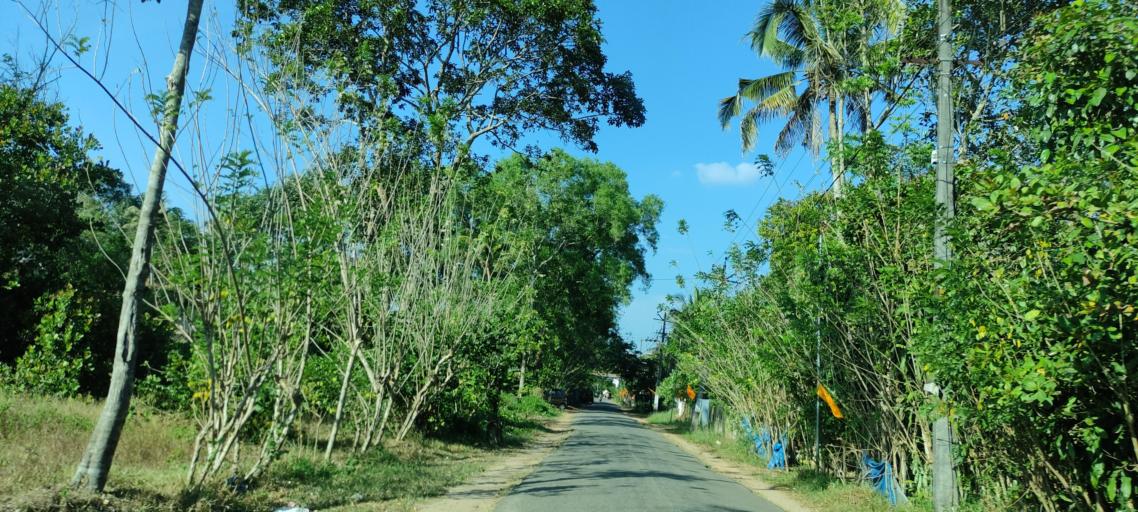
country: IN
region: Kerala
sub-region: Alappuzha
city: Shertallai
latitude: 9.6366
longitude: 76.3435
